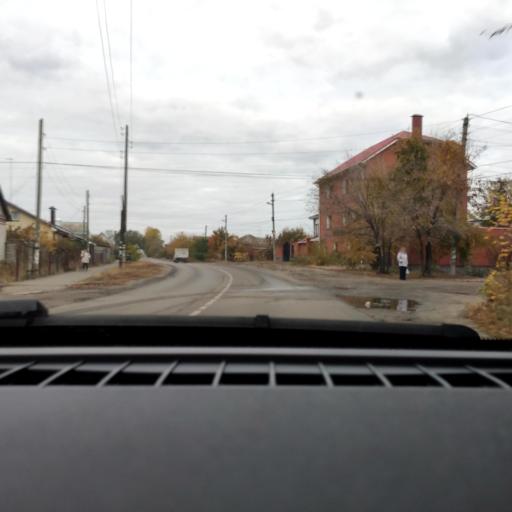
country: RU
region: Voronezj
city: Somovo
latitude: 51.7346
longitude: 39.2769
